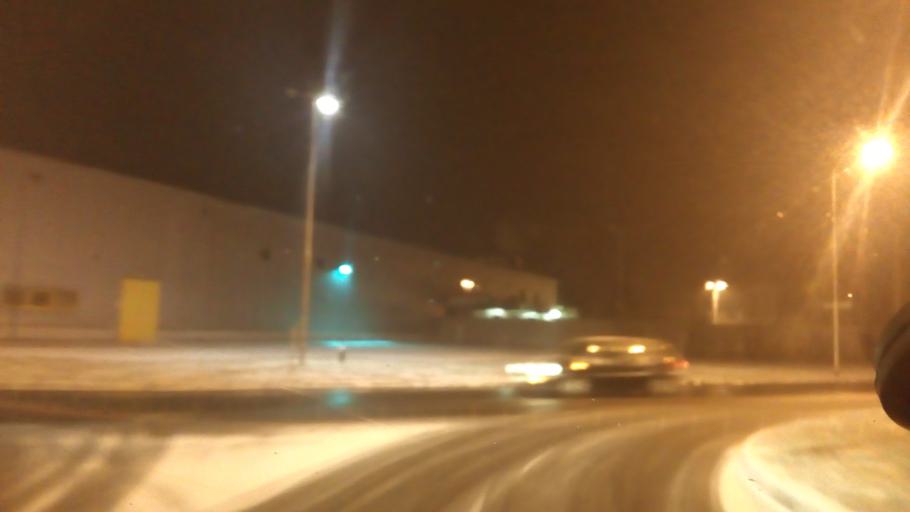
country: CZ
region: Moravskoslezsky
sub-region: Okres Frydek-Mistek
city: Stare Mesto
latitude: 49.6768
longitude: 18.3683
